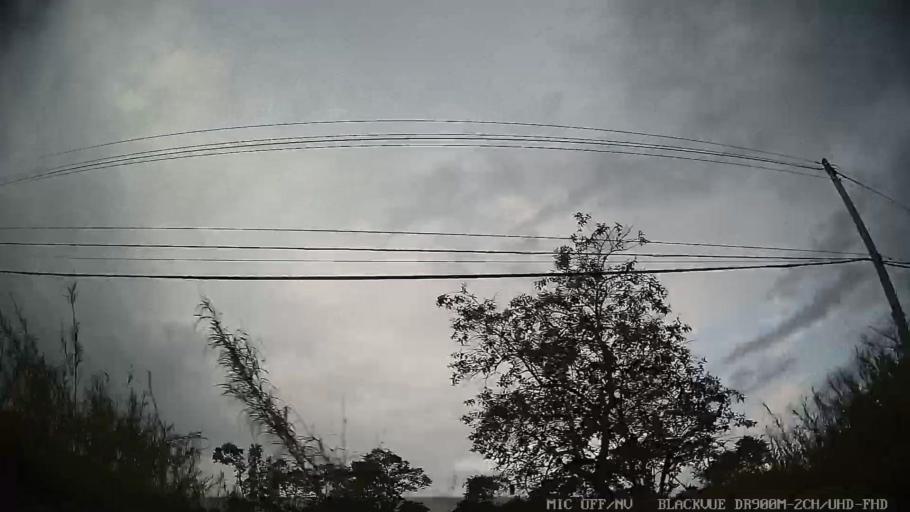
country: BR
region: Sao Paulo
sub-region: Itatiba
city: Itatiba
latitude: -23.0046
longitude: -46.8770
